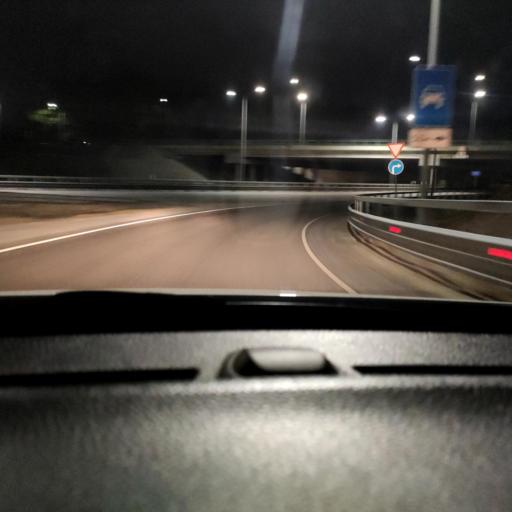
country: RU
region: Voronezj
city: Somovo
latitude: 51.6912
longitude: 39.3039
